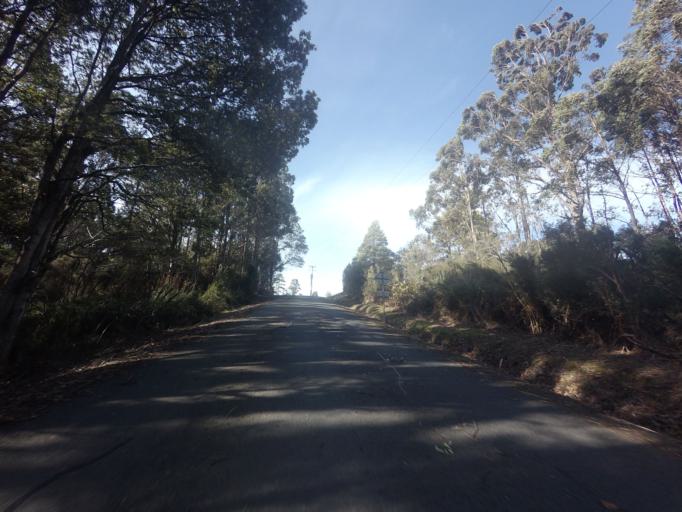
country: AU
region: Tasmania
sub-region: Kingborough
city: Kettering
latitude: -43.1681
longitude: 147.1864
